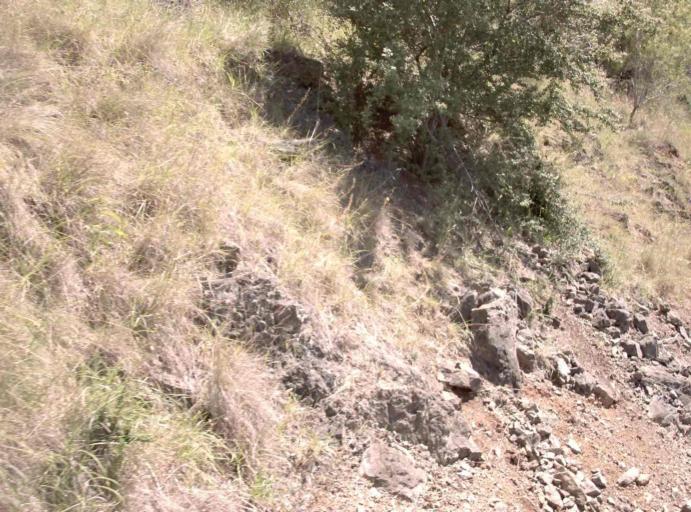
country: AU
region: Victoria
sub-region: East Gippsland
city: Lakes Entrance
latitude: -37.4069
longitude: 148.2111
